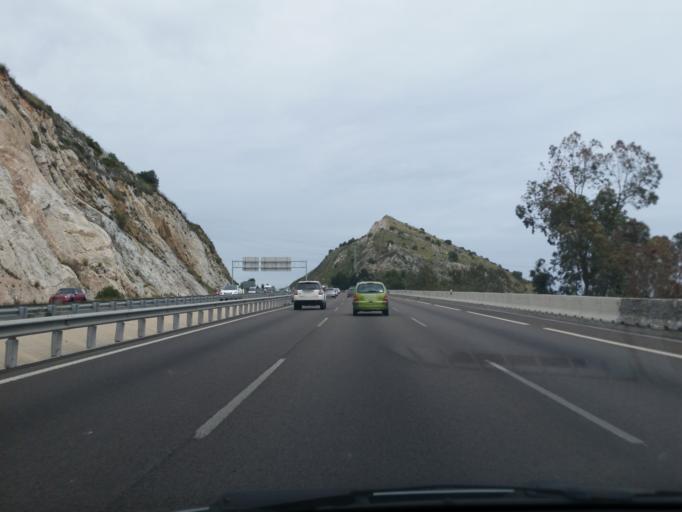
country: ES
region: Andalusia
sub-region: Provincia de Malaga
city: Benalmadena
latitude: 36.5872
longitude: -4.5929
